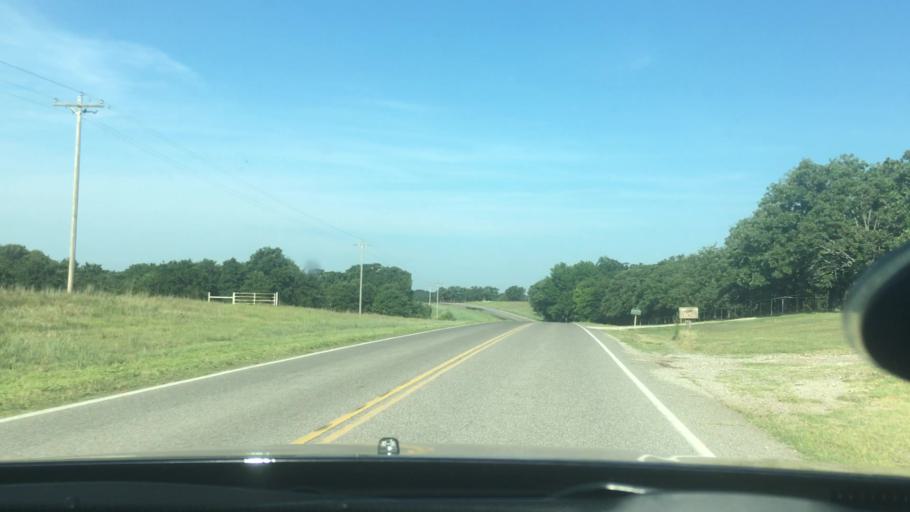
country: US
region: Oklahoma
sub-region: Garvin County
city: Pauls Valley
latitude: 34.6521
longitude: -97.3469
